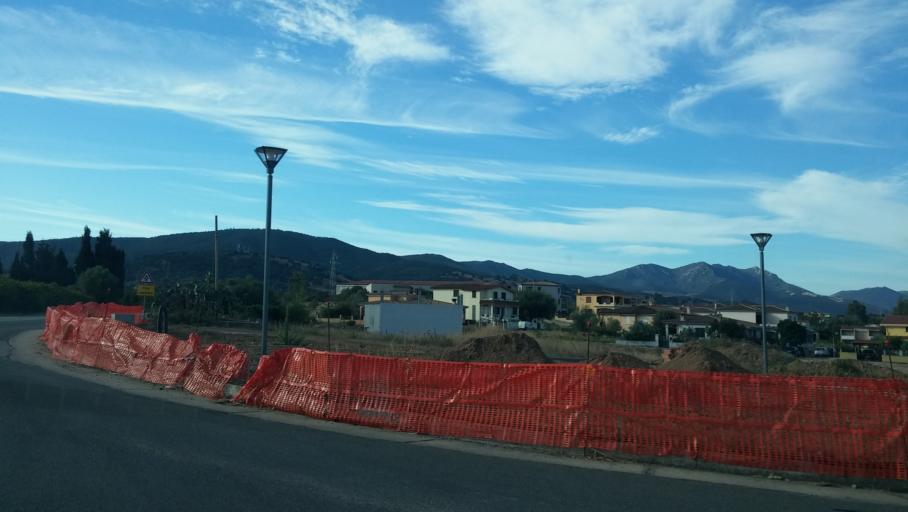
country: IT
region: Sardinia
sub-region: Provincia di Nuoro
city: Siniscola
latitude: 40.5720
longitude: 9.7101
